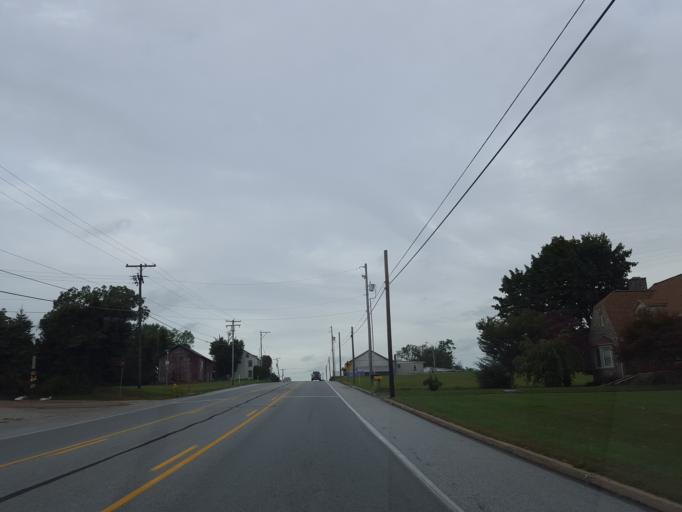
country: US
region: Pennsylvania
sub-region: York County
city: Spring Grove
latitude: 39.9189
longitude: -76.9071
